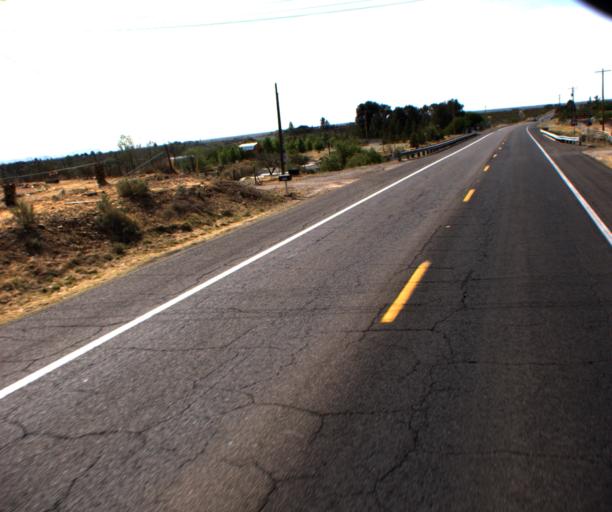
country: US
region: Arizona
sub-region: Graham County
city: Swift Trail Junction
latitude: 32.7227
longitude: -109.7110
